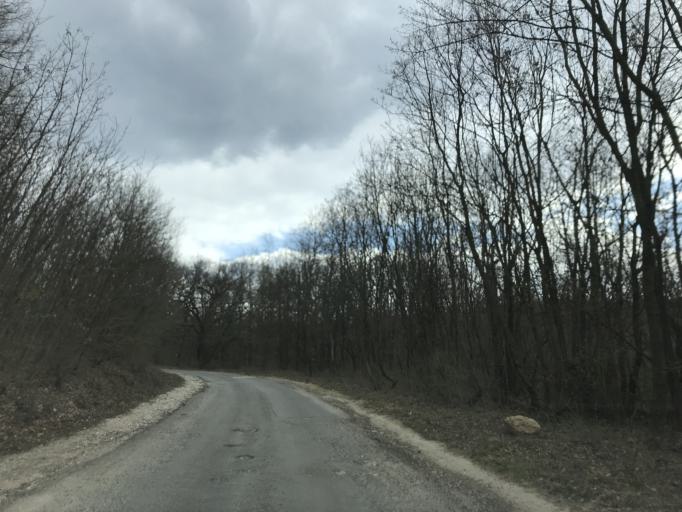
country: HU
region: Komarom-Esztergom
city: Kesztolc
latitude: 47.7053
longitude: 18.8284
